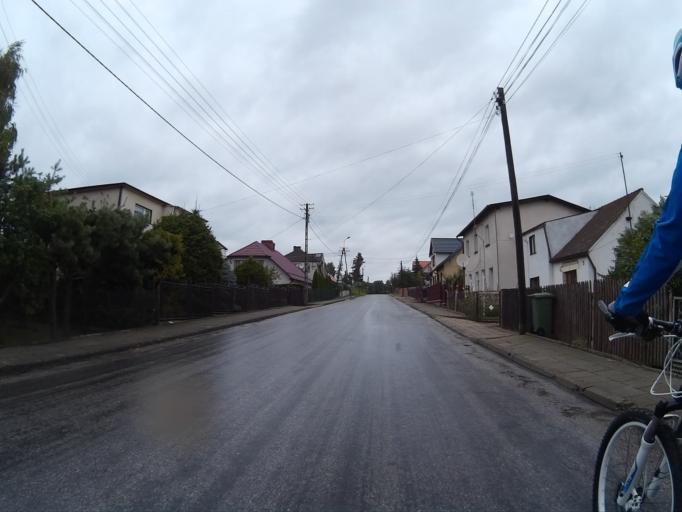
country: PL
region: Kujawsko-Pomorskie
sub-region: Powiat swiecki
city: Osie
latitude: 53.5997
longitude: 18.3526
